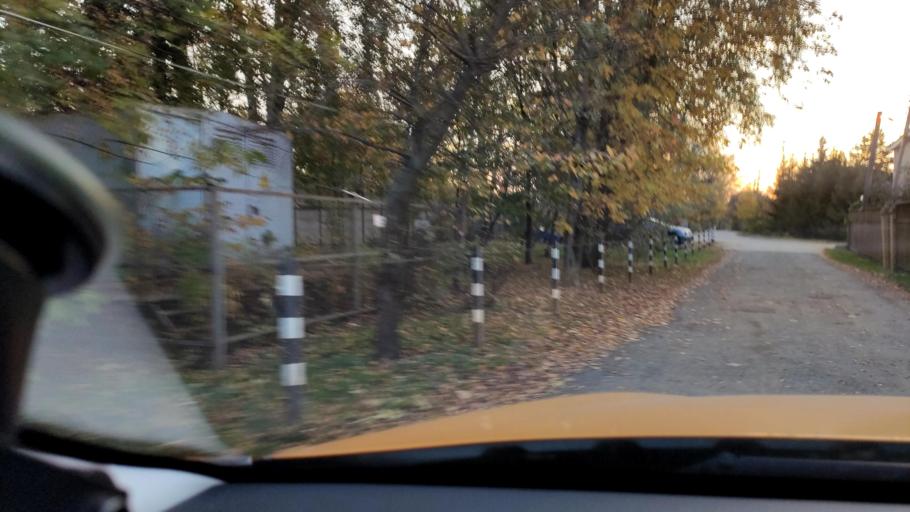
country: RU
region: Moskovskaya
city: Pirogovskiy
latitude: 55.9696
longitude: 37.6870
